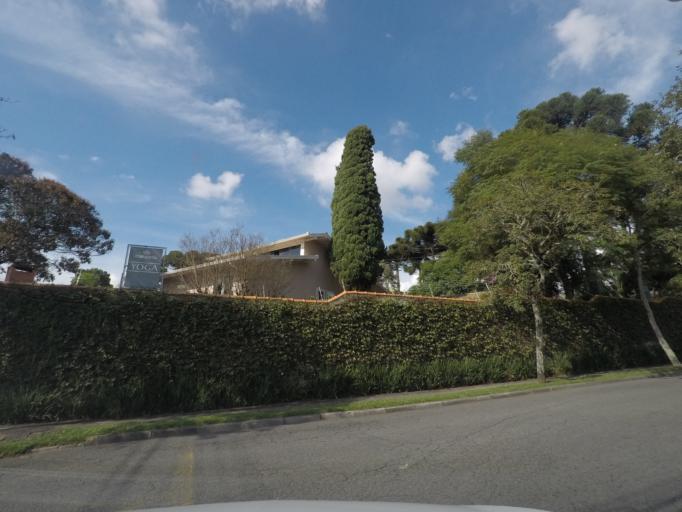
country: BR
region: Parana
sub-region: Pinhais
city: Pinhais
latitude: -25.4581
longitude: -49.2339
